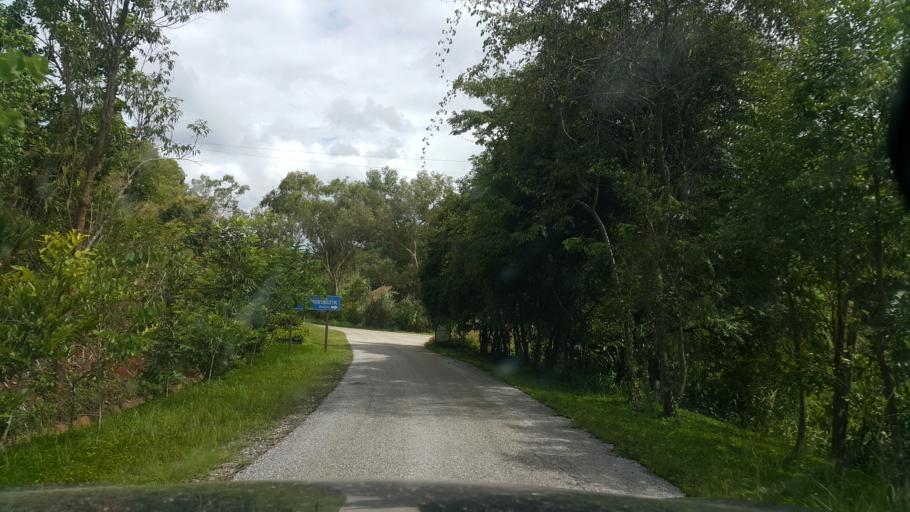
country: TH
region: Loei
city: Na Haeo
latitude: 17.5997
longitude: 100.9020
